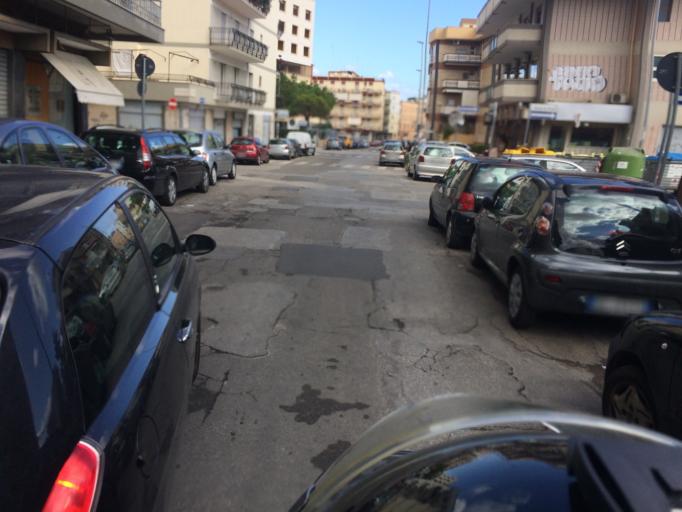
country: IT
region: Apulia
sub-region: Provincia di Bari
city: Bari
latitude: 41.1077
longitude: 16.8630
